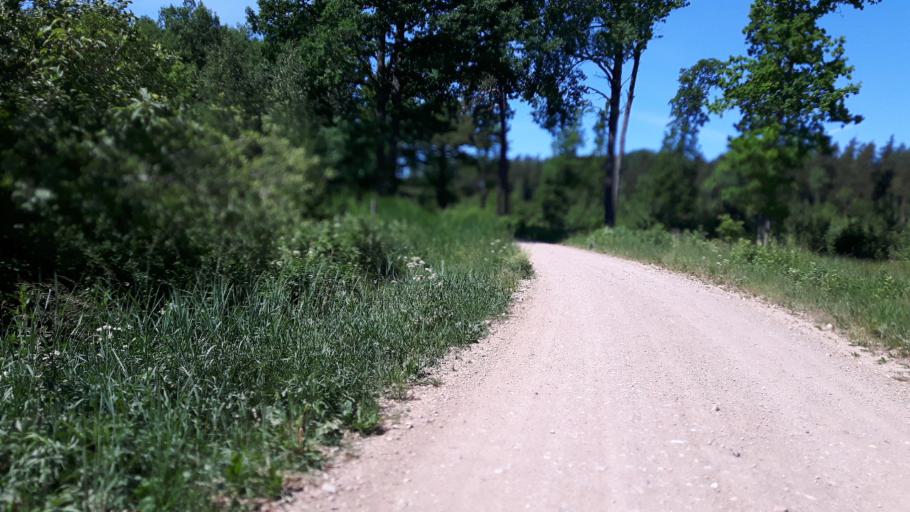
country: LV
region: Kandava
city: Kandava
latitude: 57.0428
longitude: 22.8523
